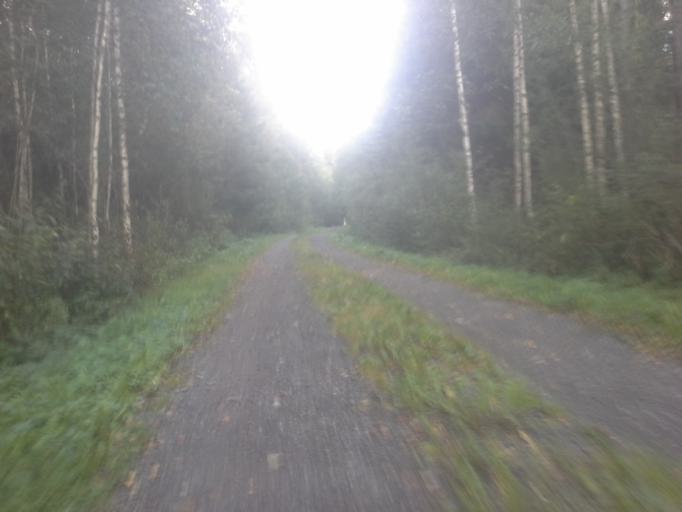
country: RU
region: Moskovskaya
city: Kievskij
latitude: 55.3582
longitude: 36.8982
